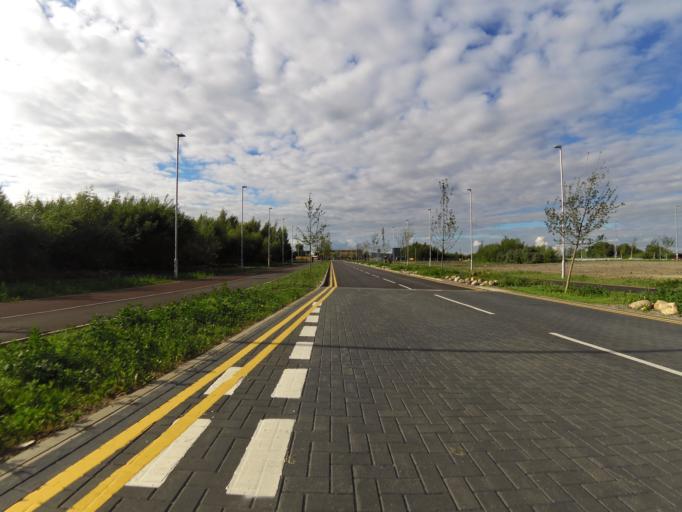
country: GB
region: England
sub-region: Cambridgeshire
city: Cambridge
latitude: 52.2253
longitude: 0.1575
